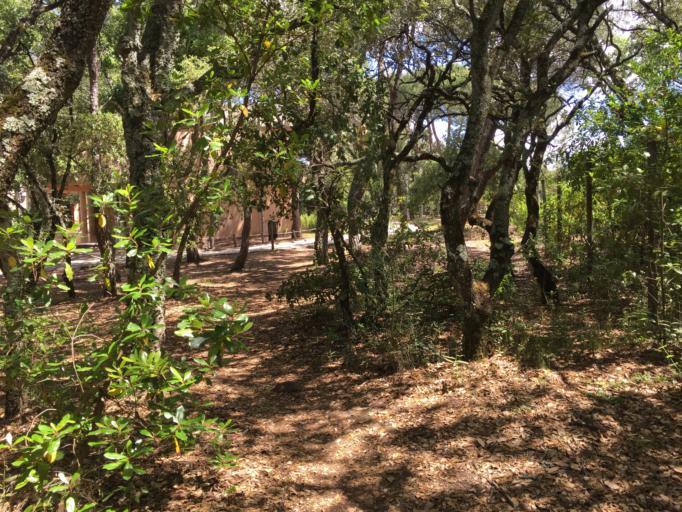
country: PT
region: Lisbon
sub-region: Odivelas
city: Pontinha
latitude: 38.7404
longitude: -9.1873
